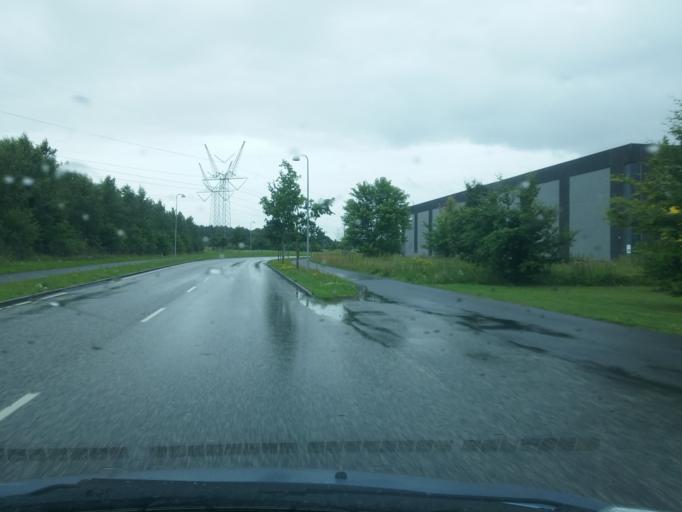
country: DK
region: South Denmark
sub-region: Odense Kommune
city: Neder Holluf
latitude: 55.3643
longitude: 10.4994
